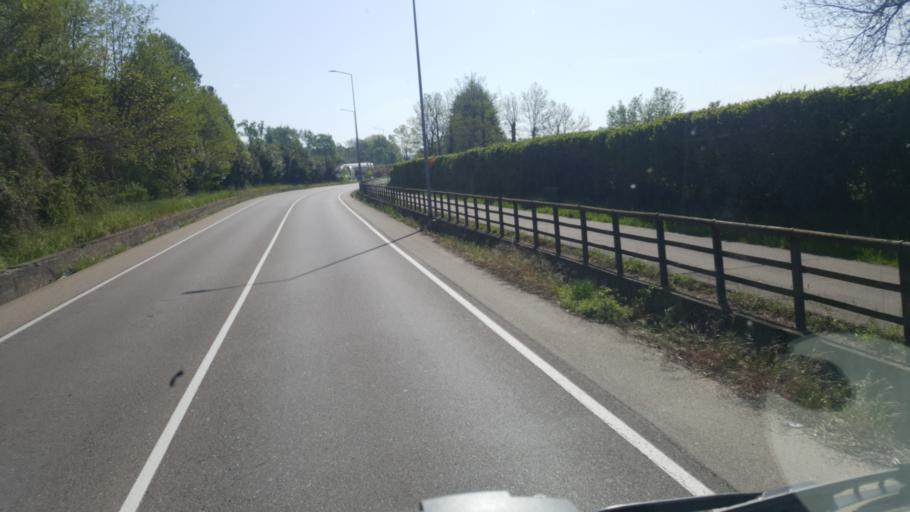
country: IT
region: Lombardy
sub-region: Provincia di Varese
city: Casciago
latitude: 45.8107
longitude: 8.7708
